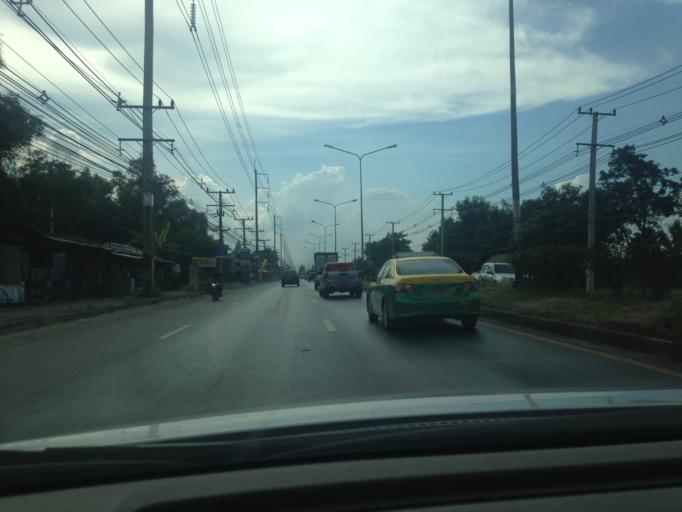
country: TH
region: Pathum Thani
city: Khlong Luang
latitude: 14.0666
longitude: 100.6842
